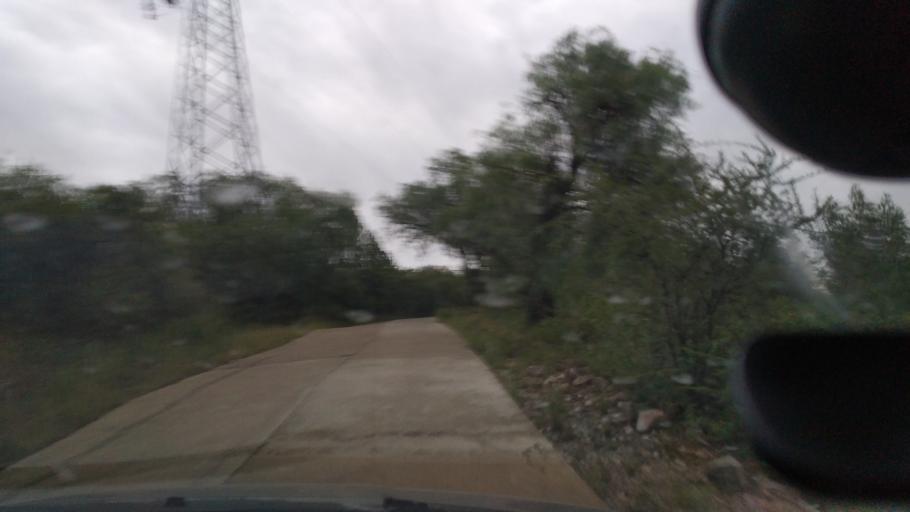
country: AR
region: Cordoba
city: Villa Las Rosas
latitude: -31.8780
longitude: -65.0230
